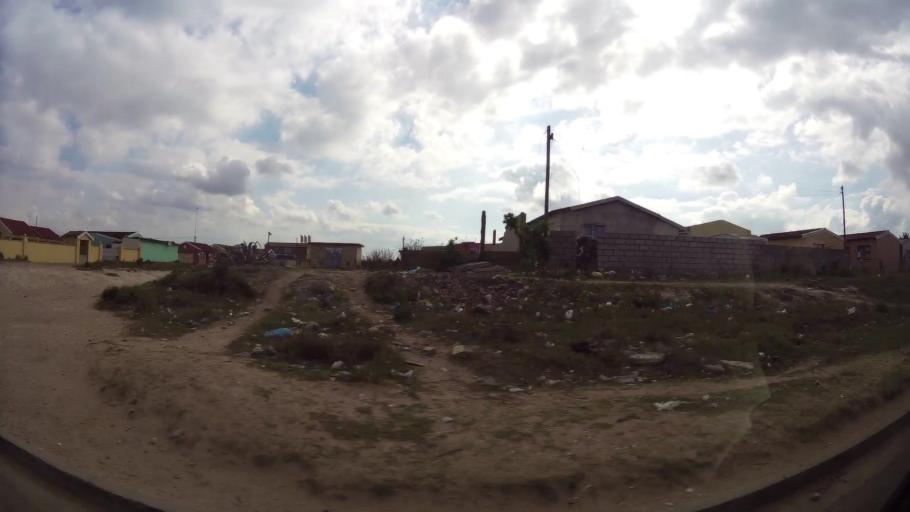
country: ZA
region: Eastern Cape
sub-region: Nelson Mandela Bay Metropolitan Municipality
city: Port Elizabeth
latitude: -33.8211
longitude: 25.5916
